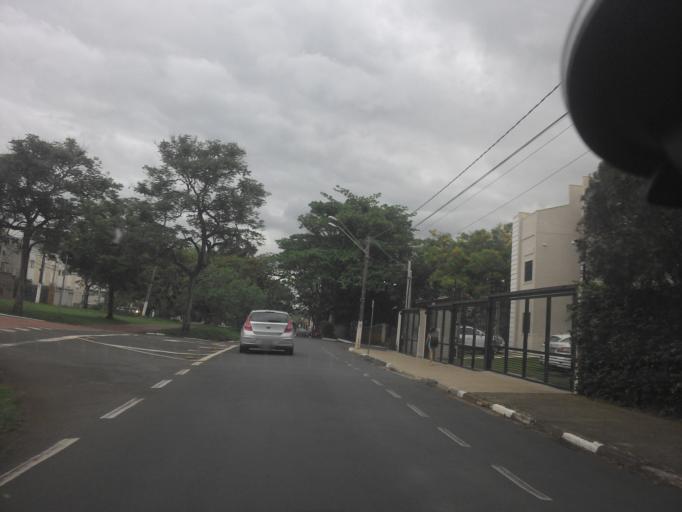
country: BR
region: Sao Paulo
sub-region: Campinas
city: Campinas
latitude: -22.8211
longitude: -47.0760
